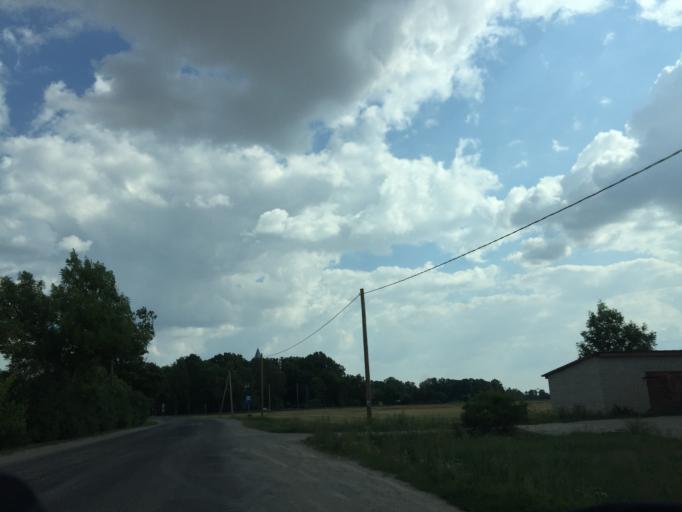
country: LV
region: Jelgava
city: Jelgava
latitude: 56.5126
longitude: 23.7540
